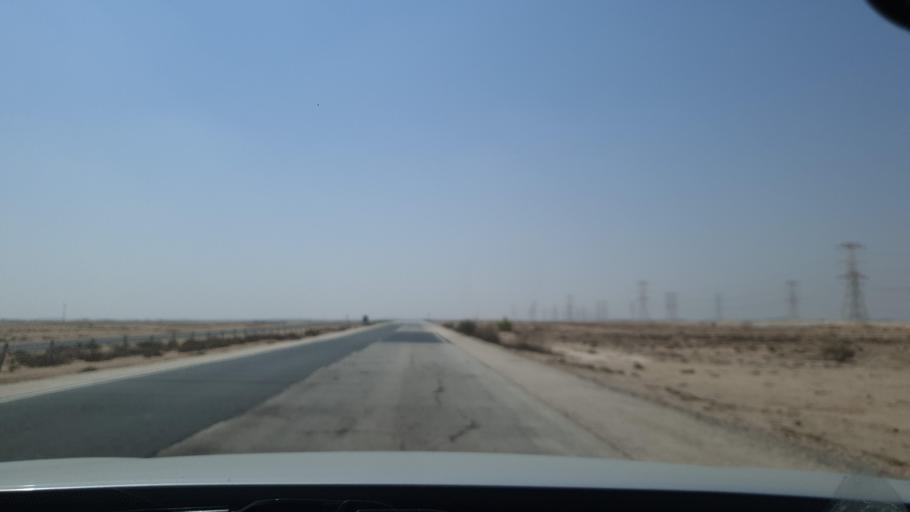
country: QA
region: Al Khawr
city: Al Khawr
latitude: 25.7123
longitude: 51.4483
